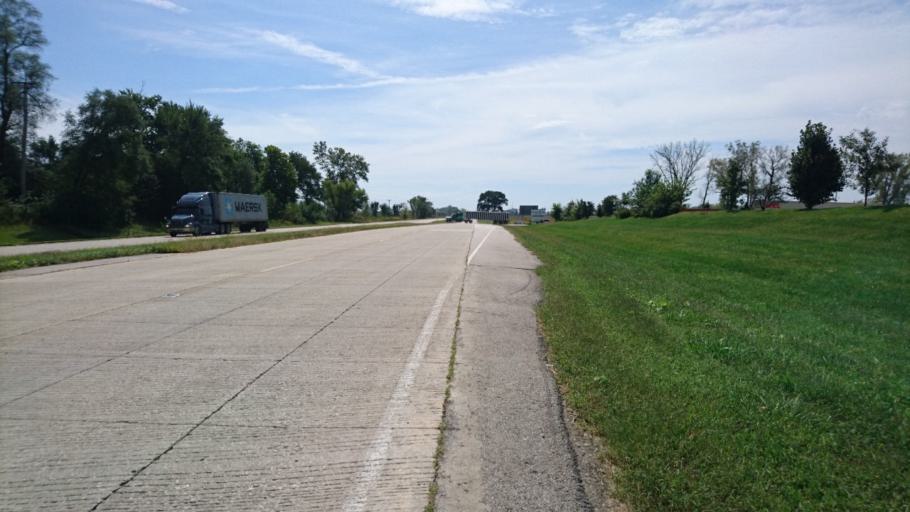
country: US
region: Illinois
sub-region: Will County
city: Wilmington
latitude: 41.3507
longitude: -88.1338
